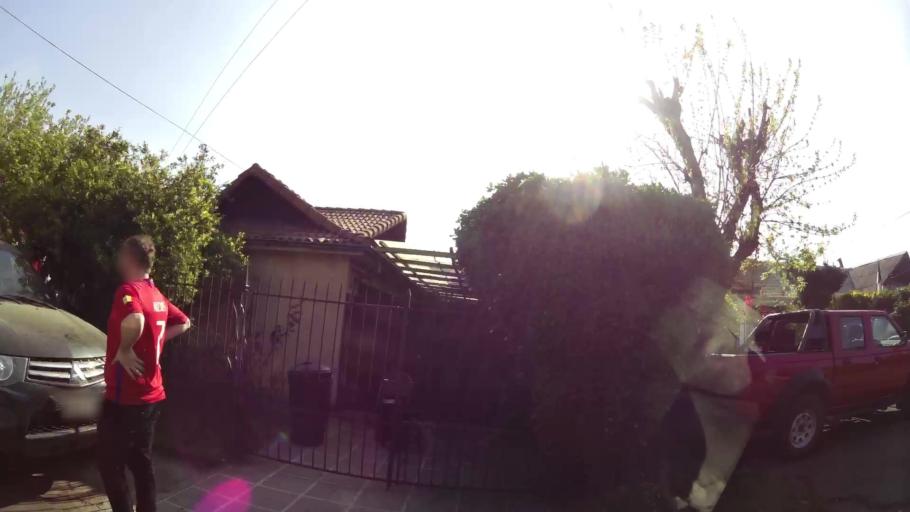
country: CL
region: Santiago Metropolitan
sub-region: Provincia de Santiago
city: Villa Presidente Frei, Nunoa, Santiago, Chile
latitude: -33.4596
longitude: -70.5735
